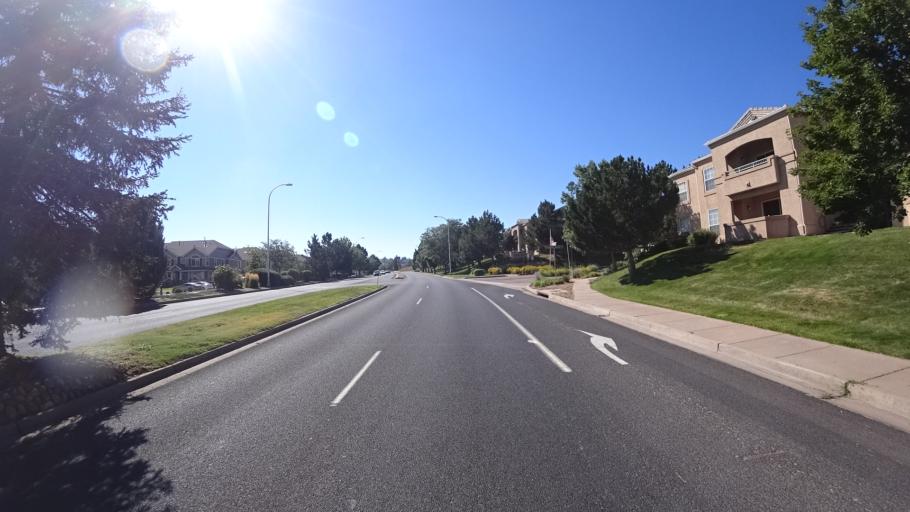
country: US
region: Colorado
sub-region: El Paso County
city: Cimarron Hills
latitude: 38.9262
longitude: -104.7516
